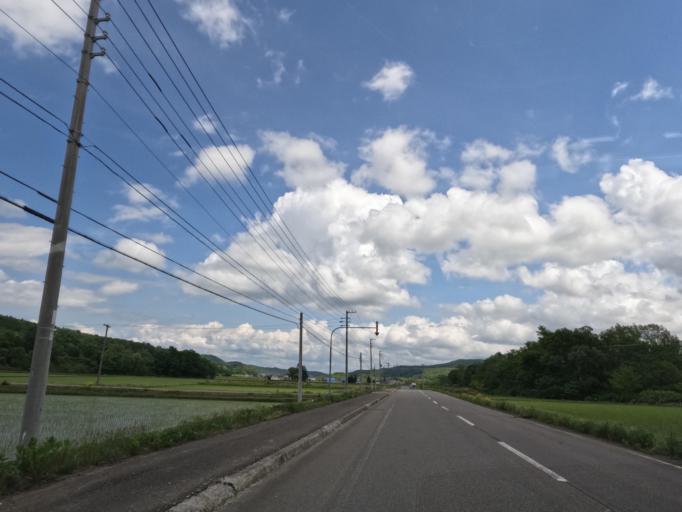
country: JP
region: Hokkaido
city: Takikawa
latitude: 43.5876
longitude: 141.7667
